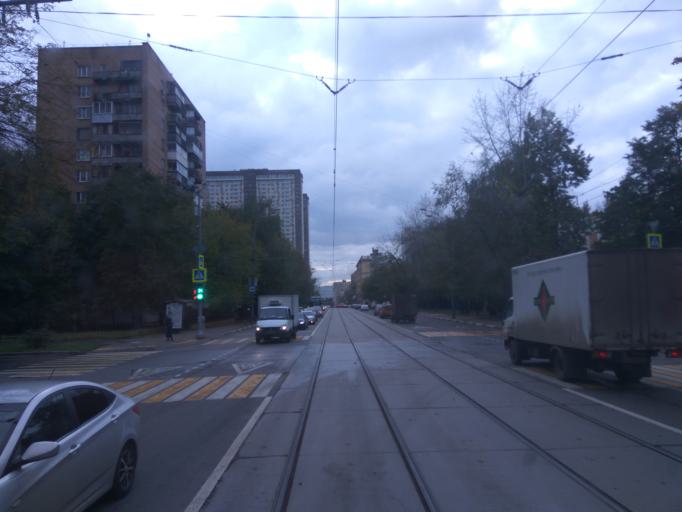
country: RU
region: Moskovskaya
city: Izmaylovo
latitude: 55.7932
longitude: 37.7944
